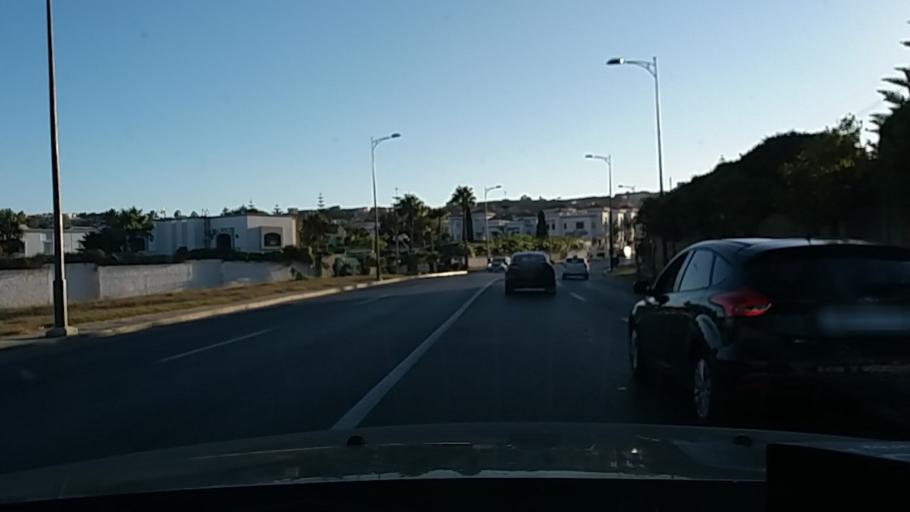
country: MA
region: Tanger-Tetouan
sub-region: Tanger-Assilah
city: Tangier
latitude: 35.7764
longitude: -5.8541
